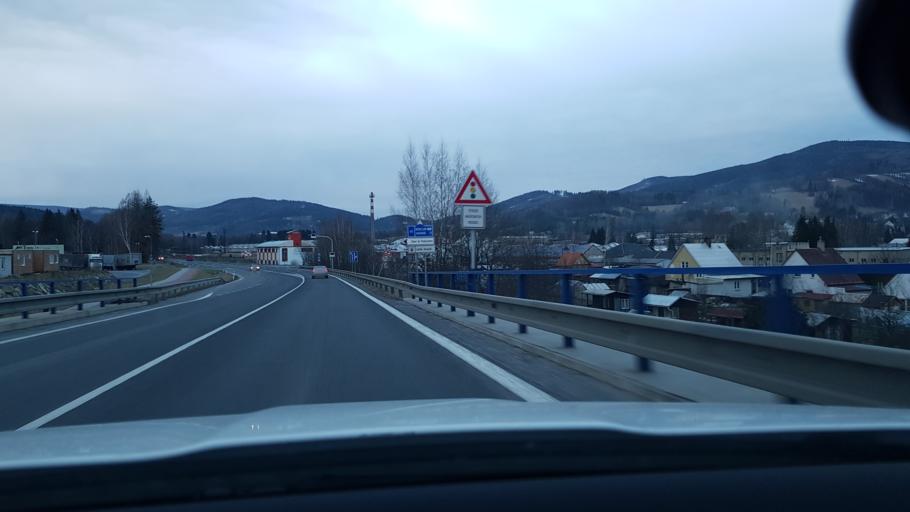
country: CZ
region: Olomoucky
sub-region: Okres Jesenik
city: Jesenik
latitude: 50.2202
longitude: 17.1921
